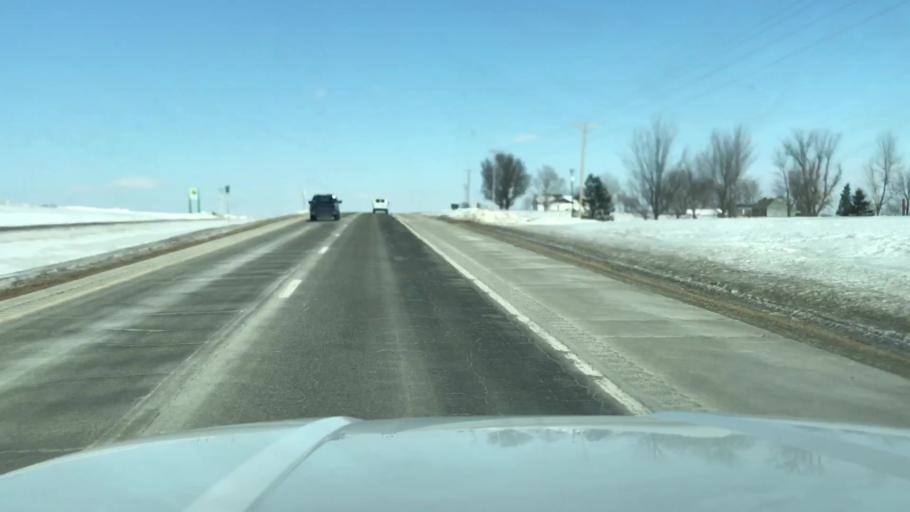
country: US
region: Missouri
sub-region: Nodaway County
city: Maryville
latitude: 40.2976
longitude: -94.8749
